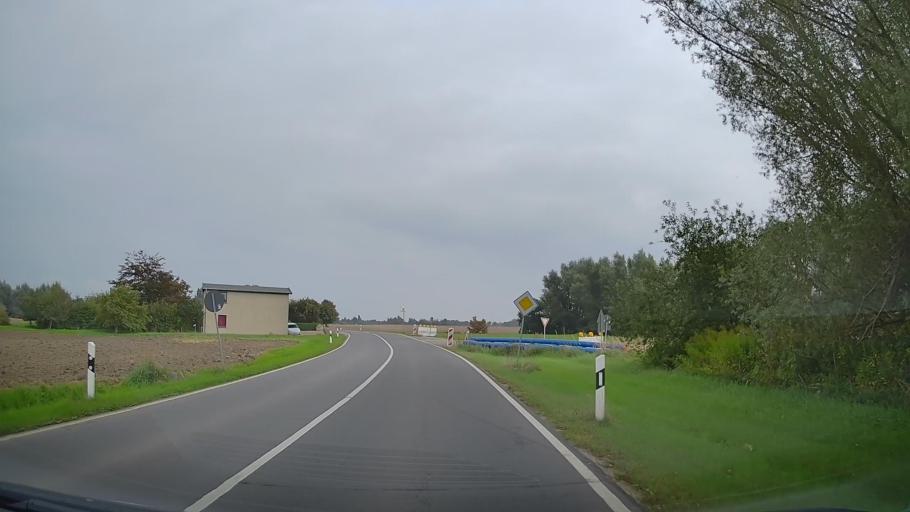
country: DE
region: Mecklenburg-Vorpommern
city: Ostseebad Kuhlungsborn
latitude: 54.1347
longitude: 11.7612
